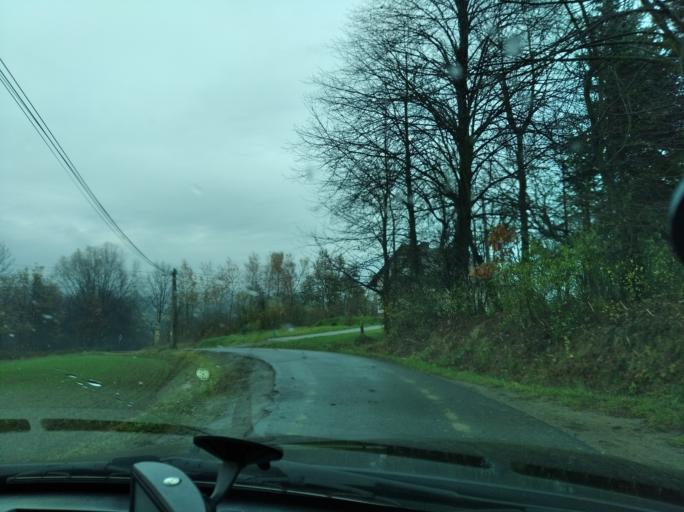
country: PL
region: Subcarpathian Voivodeship
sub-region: Powiat strzyzowski
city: Babica
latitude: 49.9308
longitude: 21.8854
